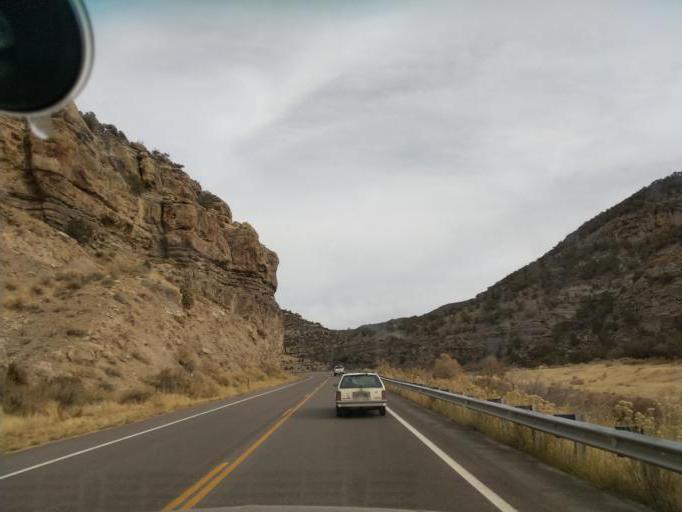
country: US
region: Colorado
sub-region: Mesa County
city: Palisade
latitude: 39.1957
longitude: -108.2250
